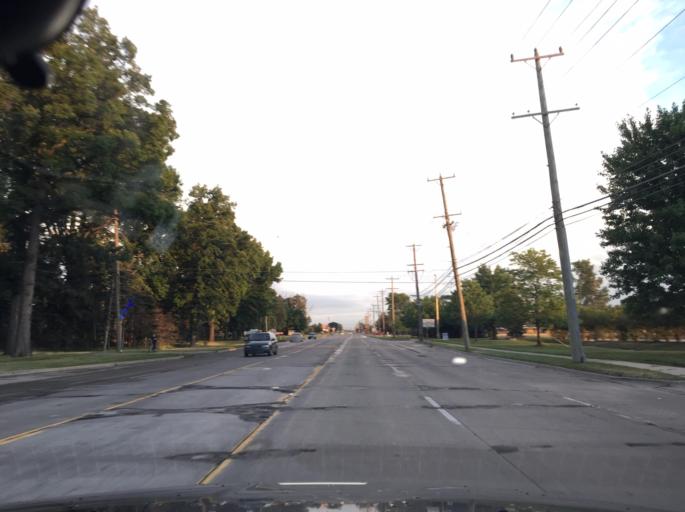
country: US
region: Michigan
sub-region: Macomb County
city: Clinton
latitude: 42.6187
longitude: -82.9532
